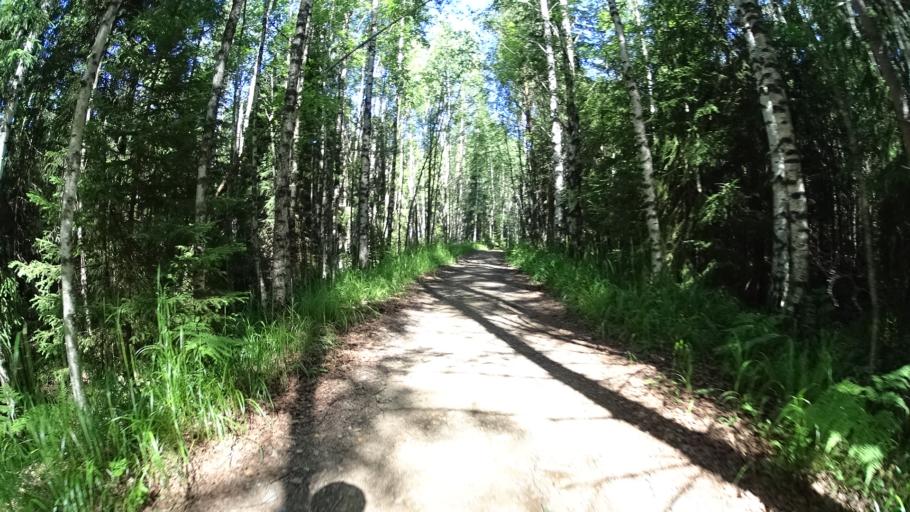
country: FI
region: Uusimaa
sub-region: Helsinki
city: Espoo
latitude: 60.3164
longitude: 24.5023
